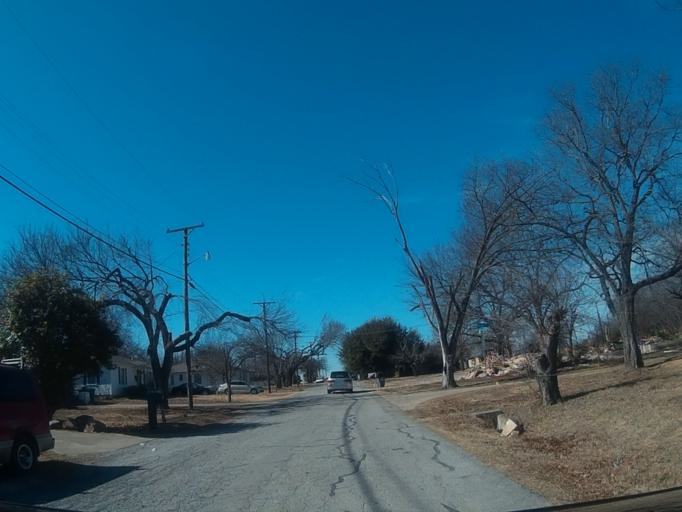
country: US
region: Texas
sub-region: Collin County
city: Allen
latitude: 33.1043
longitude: -96.6738
